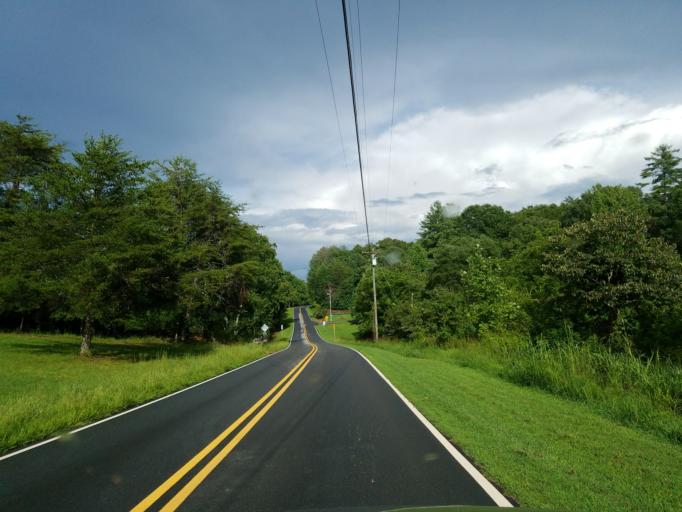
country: US
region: Georgia
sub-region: White County
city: Cleveland
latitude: 34.6369
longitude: -83.8558
